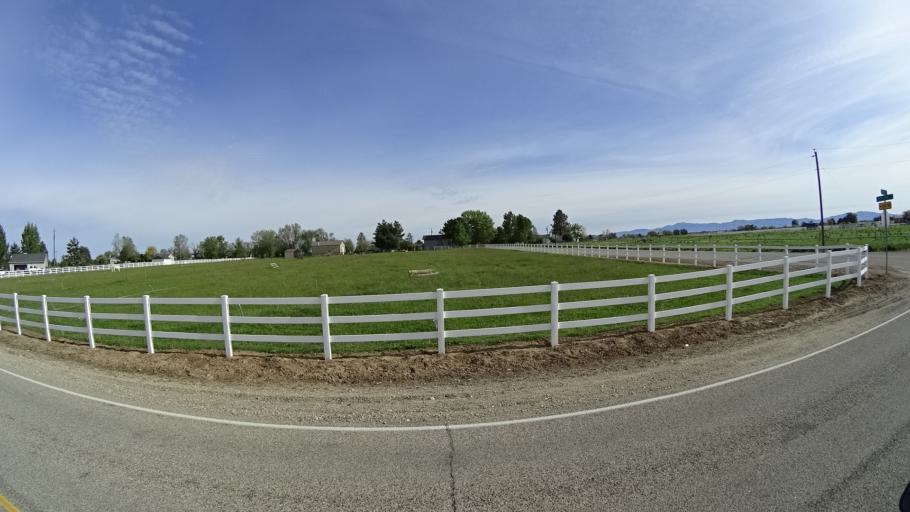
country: US
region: Idaho
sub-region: Ada County
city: Kuna
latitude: 43.4736
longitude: -116.3619
